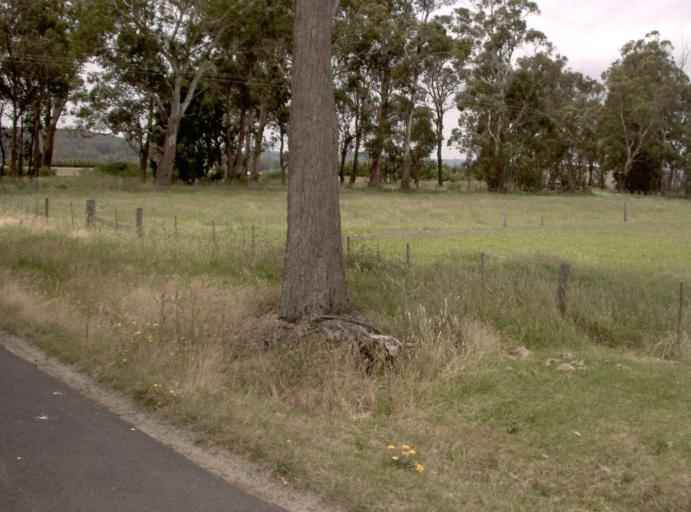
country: AU
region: Victoria
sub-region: Latrobe
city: Traralgon
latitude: -38.4875
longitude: 146.6805
